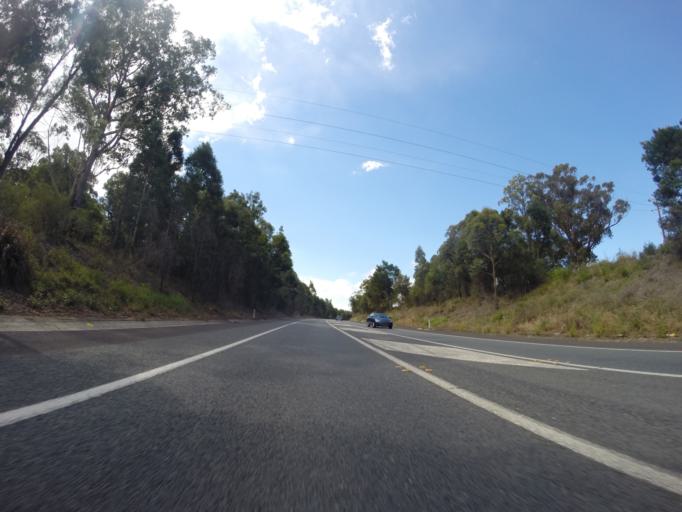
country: AU
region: New South Wales
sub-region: Shoalhaven Shire
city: Falls Creek
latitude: -35.0298
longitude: 150.5796
